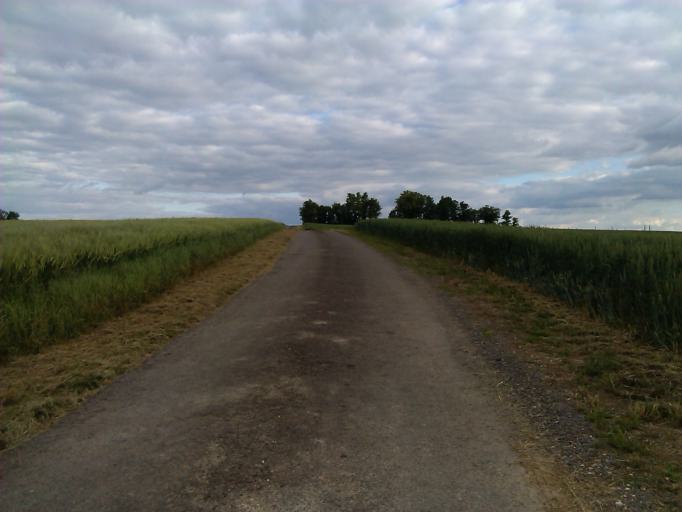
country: FR
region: Poitou-Charentes
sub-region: Departement de la Charente
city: Saint-Amant-de-Boixe
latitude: 45.7879
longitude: 0.1388
